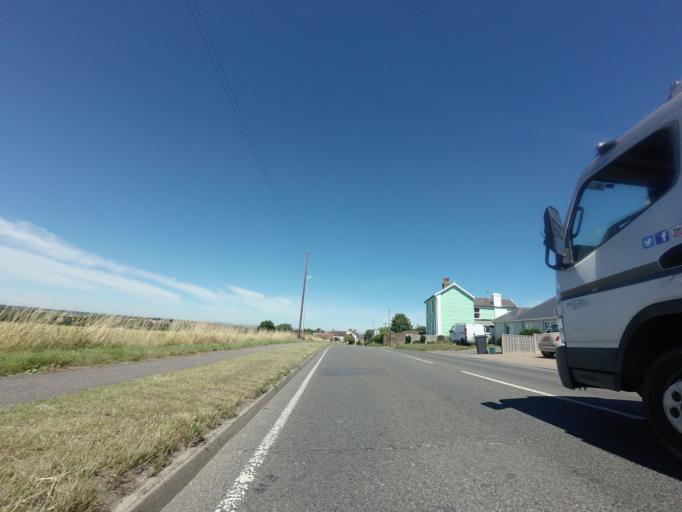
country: GB
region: England
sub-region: Kent
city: Deal
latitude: 51.1953
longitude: 1.3842
